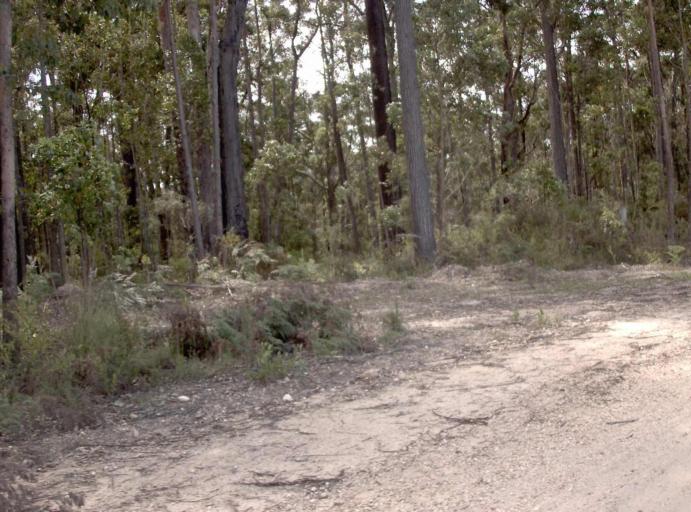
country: AU
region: Victoria
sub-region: East Gippsland
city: Lakes Entrance
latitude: -37.6245
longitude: 148.6780
